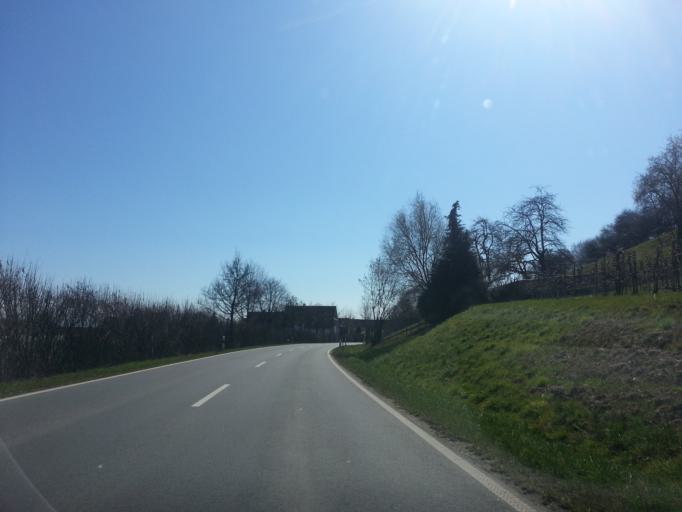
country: DE
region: Baden-Wuerttemberg
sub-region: Tuebingen Region
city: Oberteuringen
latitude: 47.6883
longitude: 9.4422
